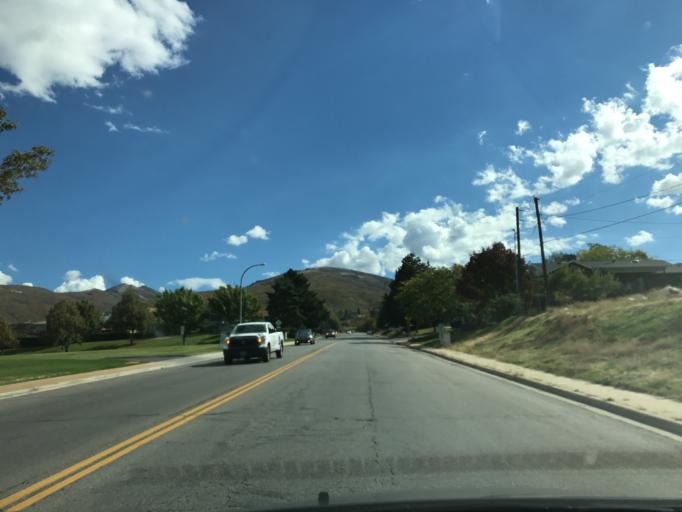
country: US
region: Utah
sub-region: Davis County
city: Bountiful
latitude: 40.8712
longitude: -111.8590
